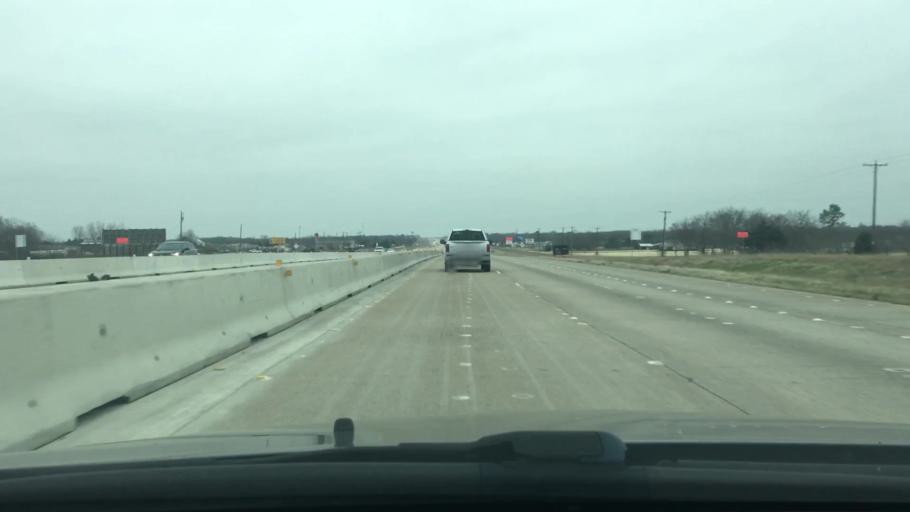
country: US
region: Texas
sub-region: Navarro County
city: Corsicana
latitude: 32.0302
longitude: -96.4428
